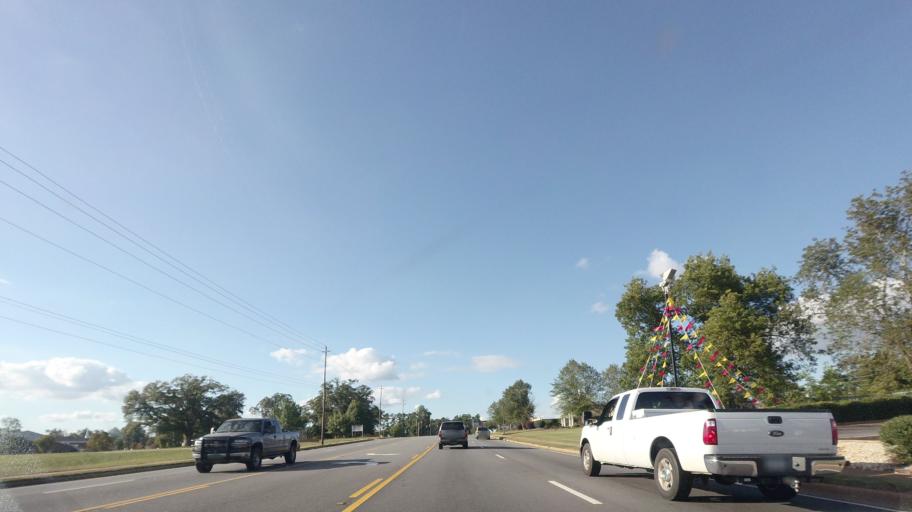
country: US
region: Georgia
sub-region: Upson County
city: Thomaston
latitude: 32.9007
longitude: -84.3288
